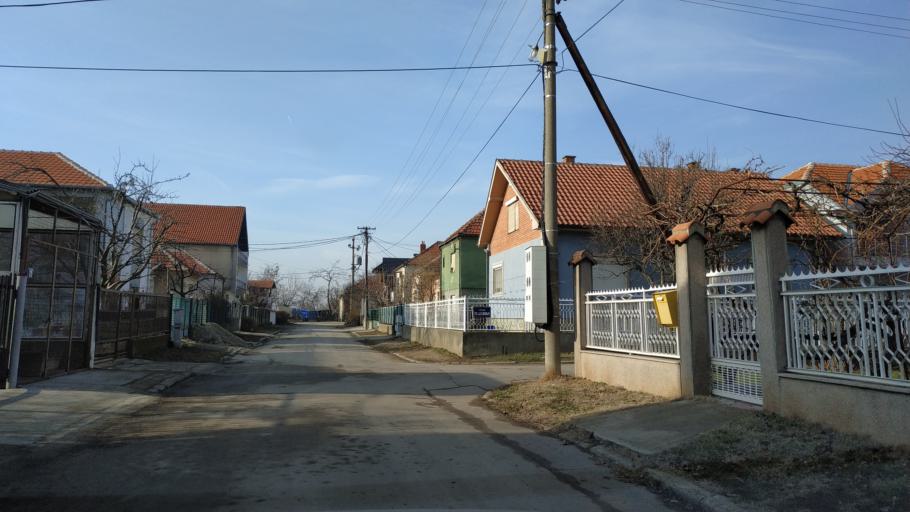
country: RS
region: Central Serbia
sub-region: Nisavski Okrug
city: Aleksinac
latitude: 43.5380
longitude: 21.6975
